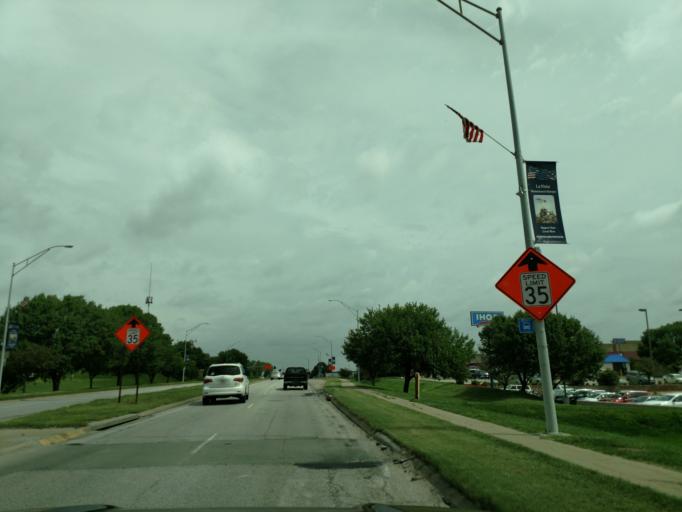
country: US
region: Nebraska
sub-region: Sarpy County
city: La Vista
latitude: 41.1874
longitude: -96.0438
